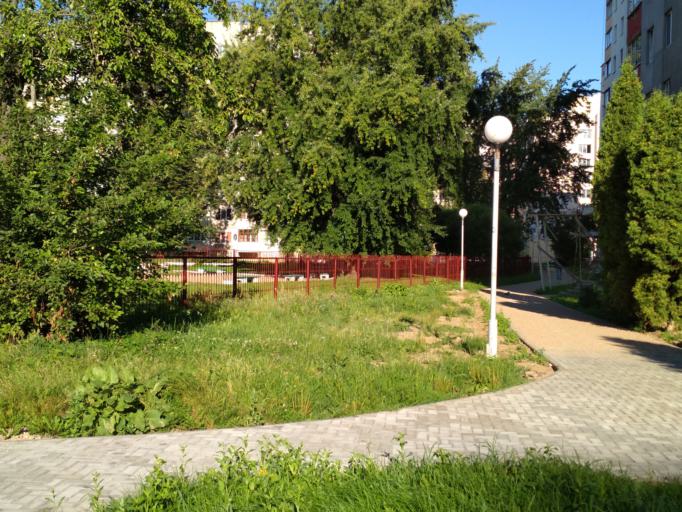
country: BY
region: Minsk
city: Minsk
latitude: 53.8810
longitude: 27.5395
